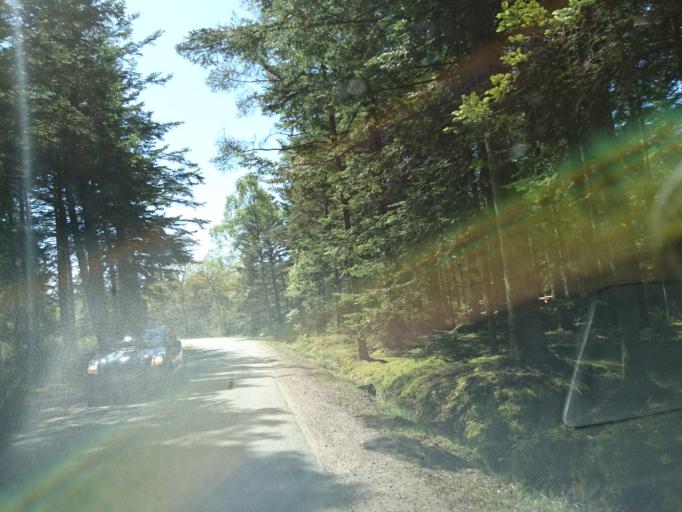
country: DK
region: North Denmark
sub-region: Hjorring Kommune
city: Sindal
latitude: 57.5972
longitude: 10.2296
